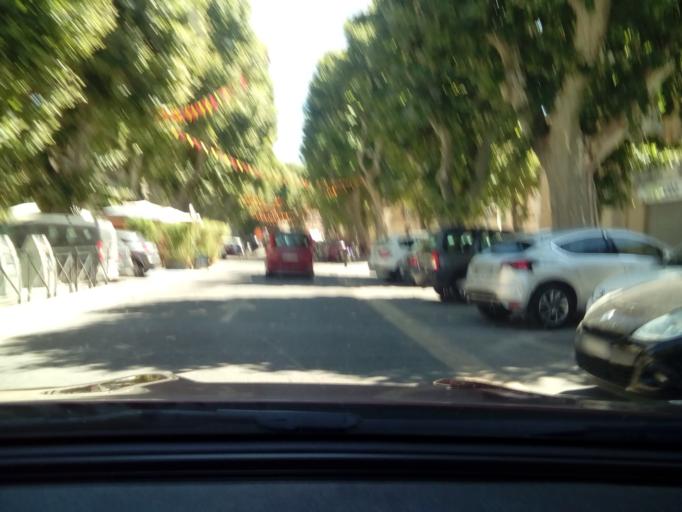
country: FR
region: Provence-Alpes-Cote d'Azur
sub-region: Departement des Bouches-du-Rhone
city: Trets
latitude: 43.4475
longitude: 5.6829
